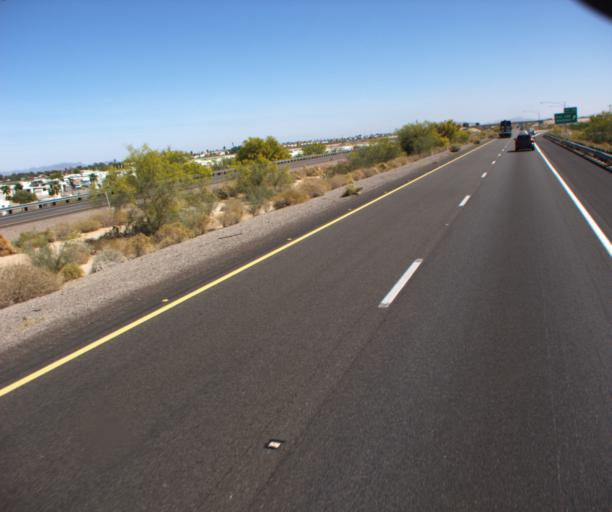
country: US
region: Arizona
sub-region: Yuma County
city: Wellton
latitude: 32.6599
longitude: -114.1498
